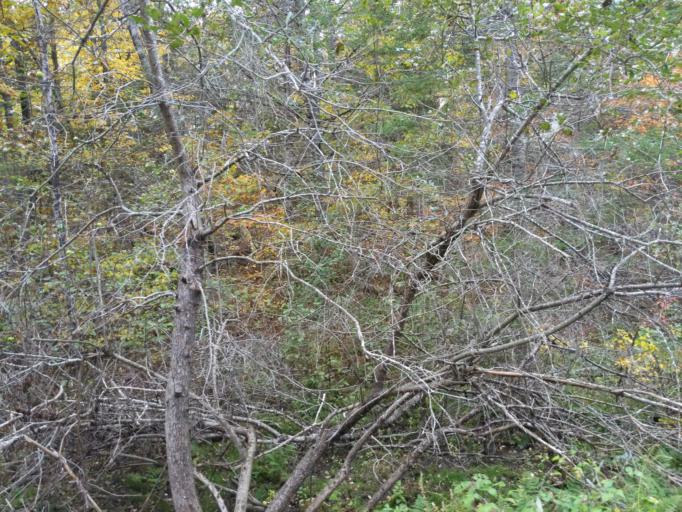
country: US
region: Maine
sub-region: Lincoln County
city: Whitefield
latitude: 44.1020
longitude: -69.6188
